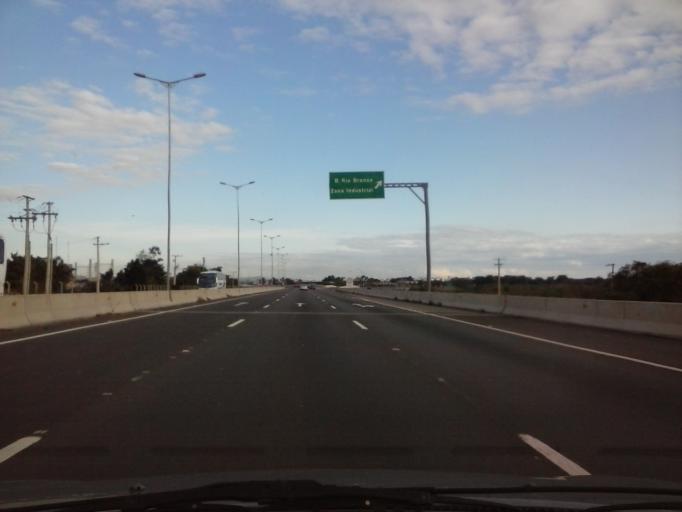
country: BR
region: Rio Grande do Sul
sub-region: Canoas
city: Canoas
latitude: -29.9595
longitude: -51.2026
